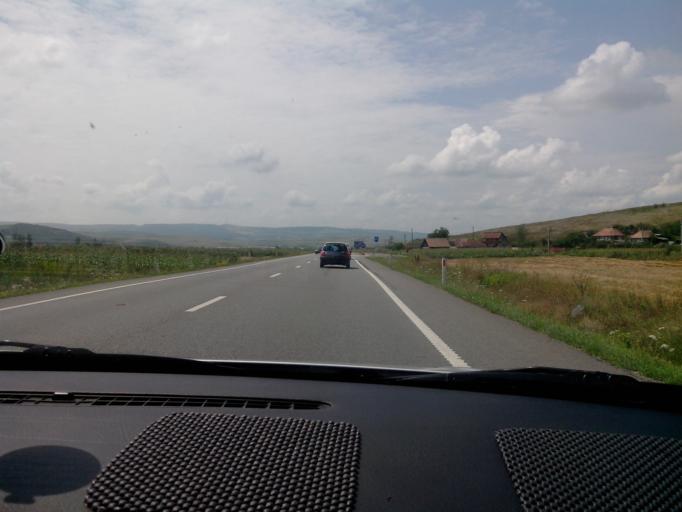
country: RO
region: Cluj
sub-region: Comuna Apahida
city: Sannicoara
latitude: 46.8017
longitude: 23.7253
